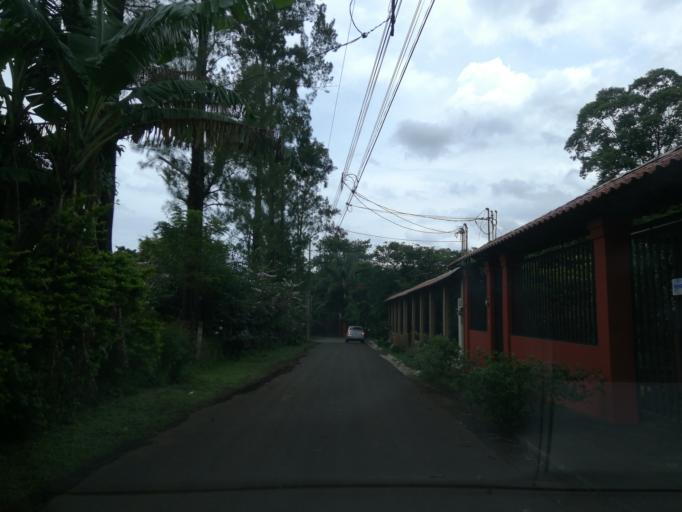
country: CR
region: Alajuela
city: Alajuela
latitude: 10.0332
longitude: -84.1866
